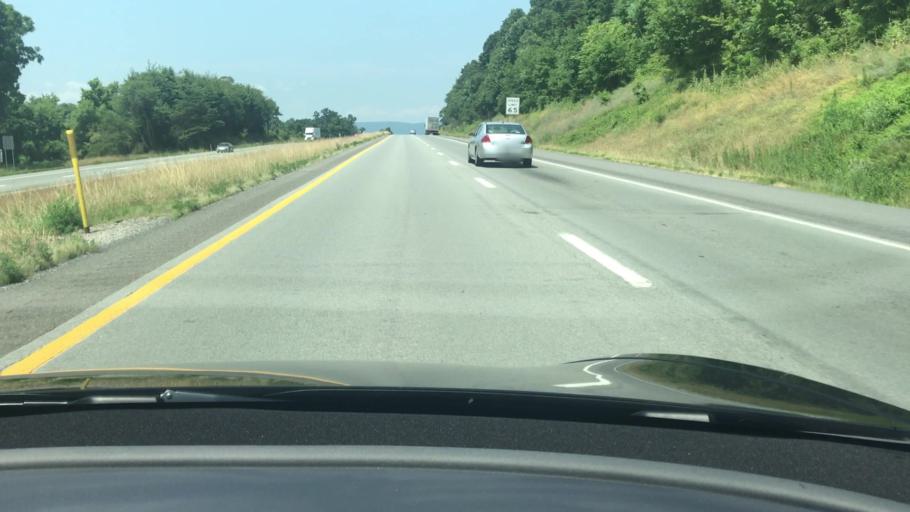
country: US
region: Pennsylvania
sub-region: Perry County
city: Newport
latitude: 40.4964
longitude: -77.1184
